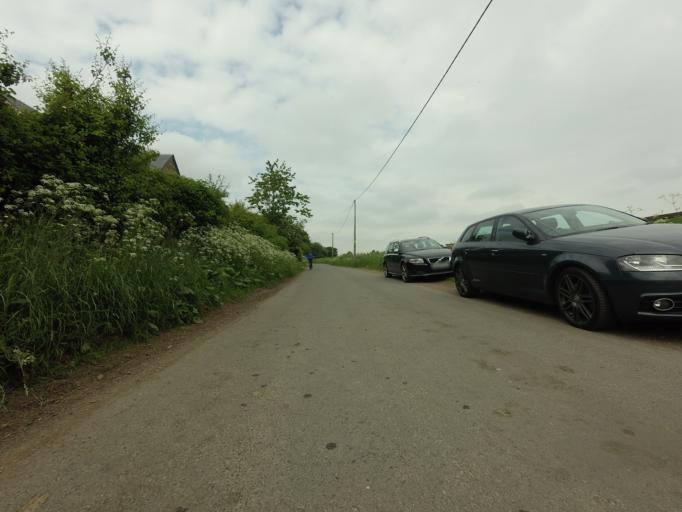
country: GB
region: Scotland
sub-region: Perth and Kinross
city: Kinross
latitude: 56.1697
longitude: -3.4462
